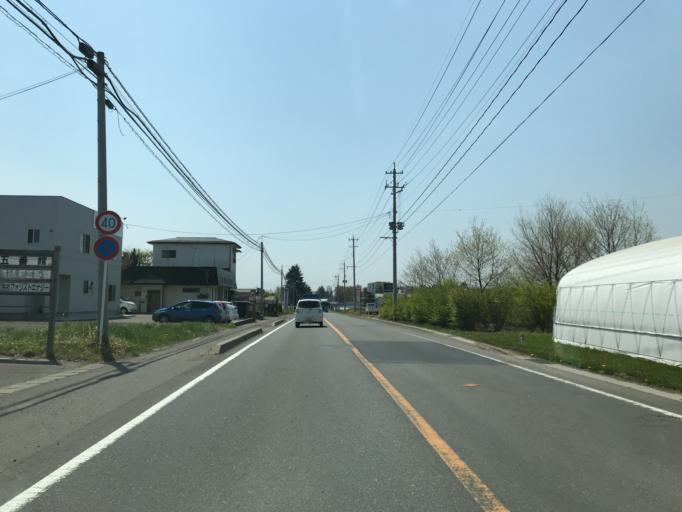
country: JP
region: Fukushima
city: Ishikawa
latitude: 37.1647
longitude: 140.3522
